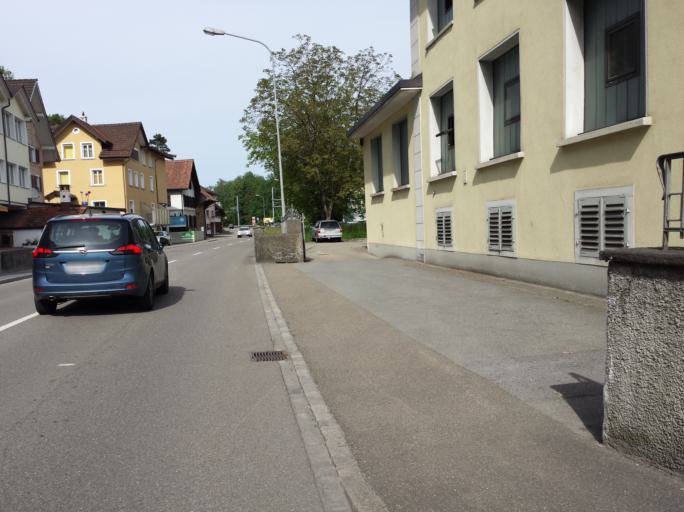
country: CH
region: Saint Gallen
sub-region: Wahlkreis Rheintal
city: Au
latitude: 47.4381
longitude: 9.6405
